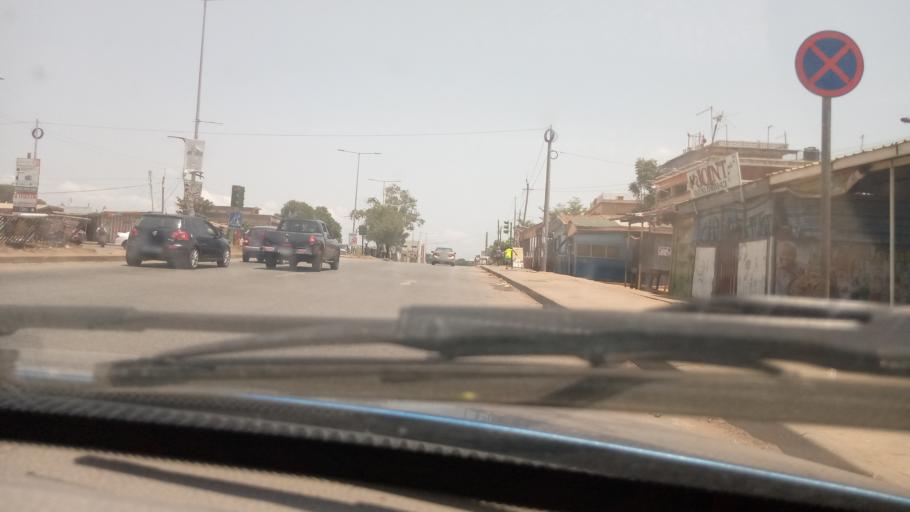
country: GH
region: Greater Accra
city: Accra
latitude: 5.5639
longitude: -0.2448
